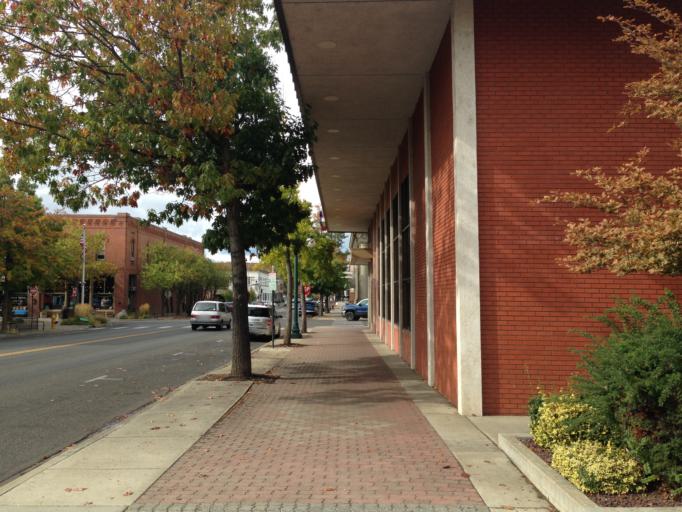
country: US
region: Washington
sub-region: Kittitas County
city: Ellensburg
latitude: 46.9967
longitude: -120.5466
